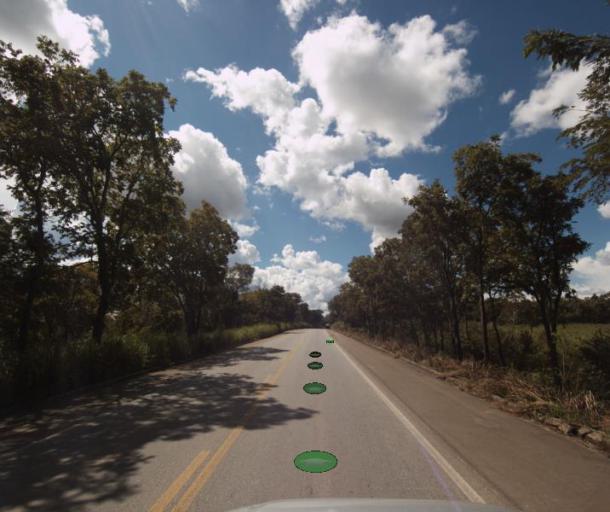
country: BR
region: Goias
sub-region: Porangatu
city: Porangatu
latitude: -13.6292
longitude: -49.0424
